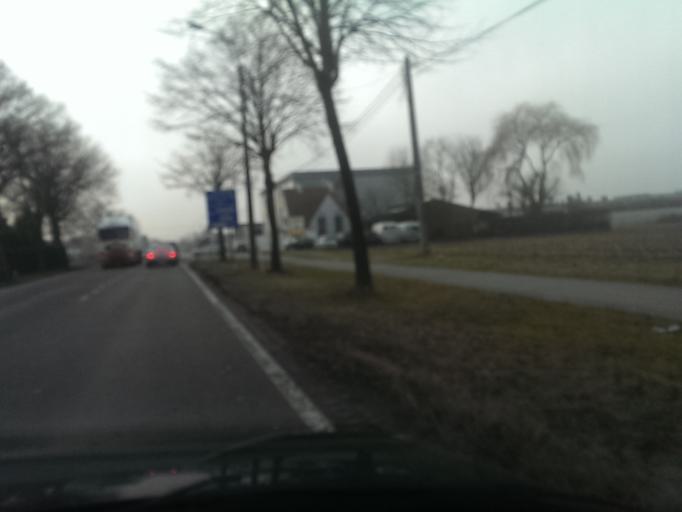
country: BE
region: Flanders
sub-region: Provincie West-Vlaanderen
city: Ledegem
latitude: 50.8655
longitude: 3.1103
